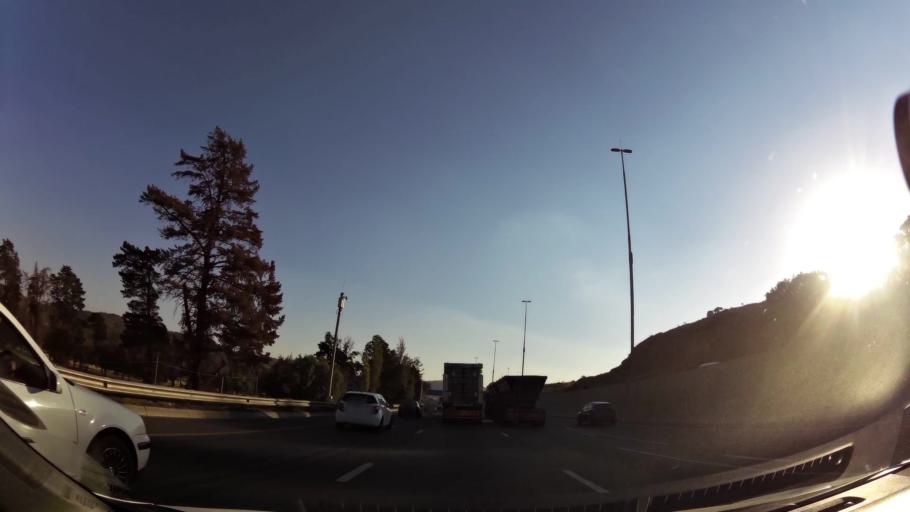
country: ZA
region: Gauteng
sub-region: Ekurhuleni Metropolitan Municipality
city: Germiston
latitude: -26.2610
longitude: 28.1067
